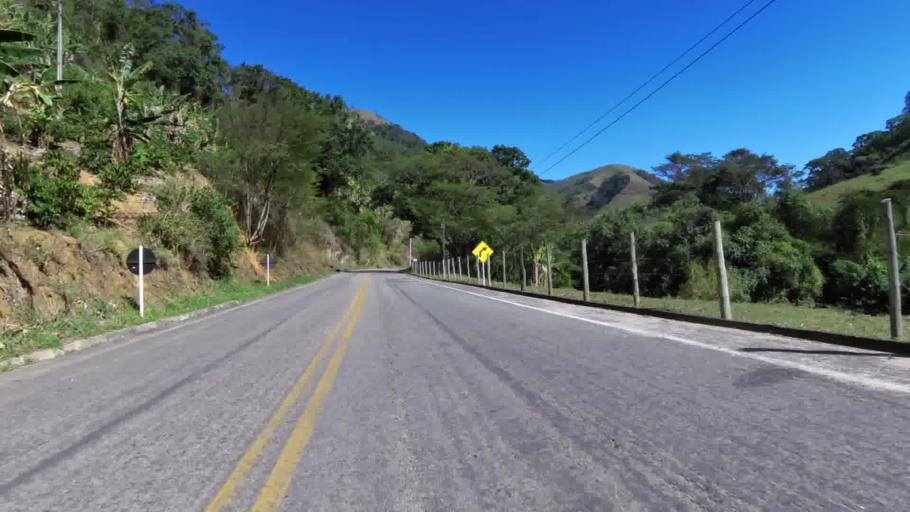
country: BR
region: Espirito Santo
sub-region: Iconha
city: Iconha
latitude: -20.7483
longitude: -40.8575
